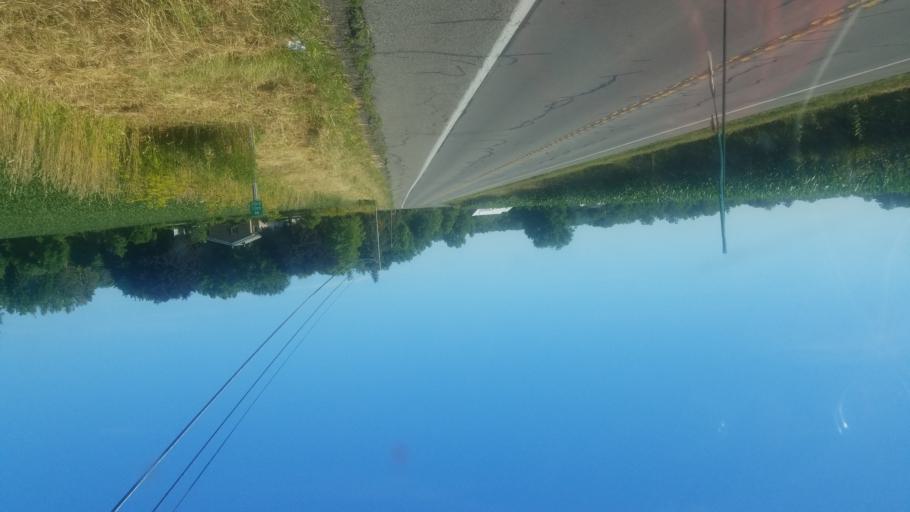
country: US
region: New York
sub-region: Ontario County
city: Phelps
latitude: 42.9912
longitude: -77.0895
